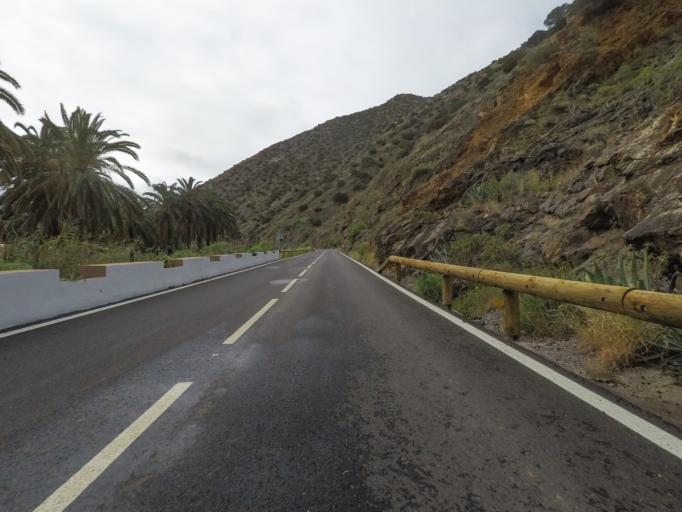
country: ES
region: Canary Islands
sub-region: Provincia de Santa Cruz de Tenerife
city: Vallehermosa
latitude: 28.1953
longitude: -17.2594
